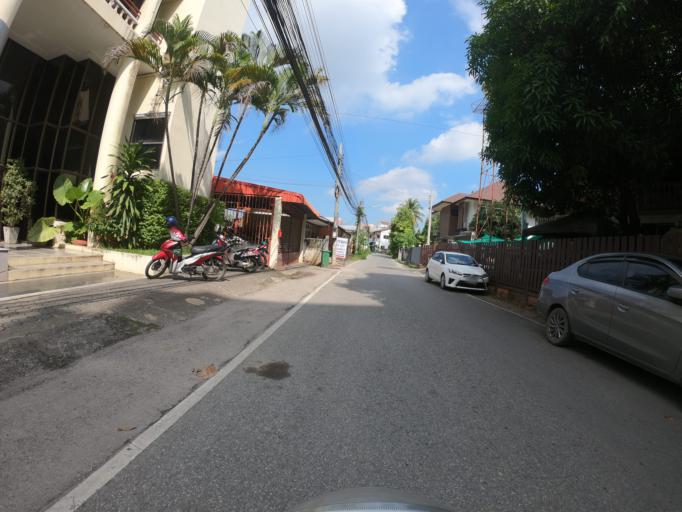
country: TH
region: Chiang Mai
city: Chiang Mai
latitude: 18.8056
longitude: 98.9691
